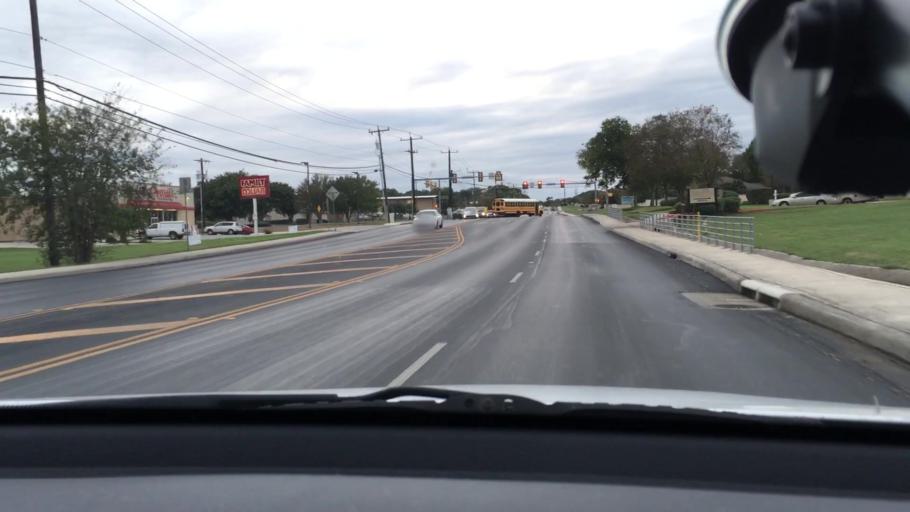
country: US
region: Texas
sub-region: Bexar County
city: Windcrest
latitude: 29.5217
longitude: -98.3532
